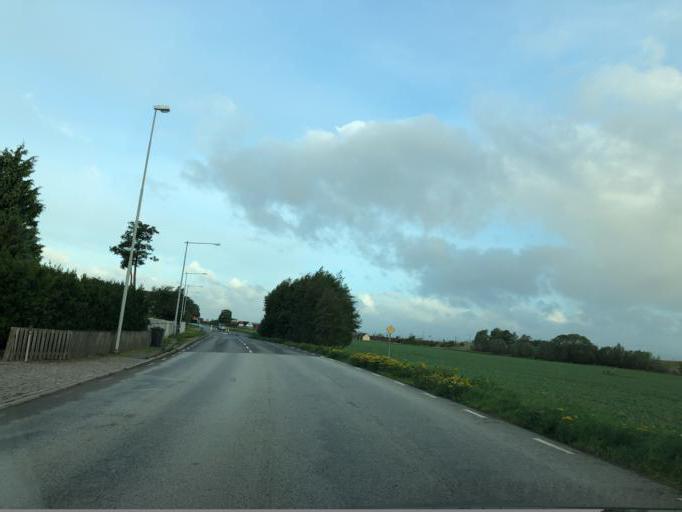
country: SE
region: Skane
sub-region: Landskrona
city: Asmundtorp
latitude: 55.8606
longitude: 12.8990
